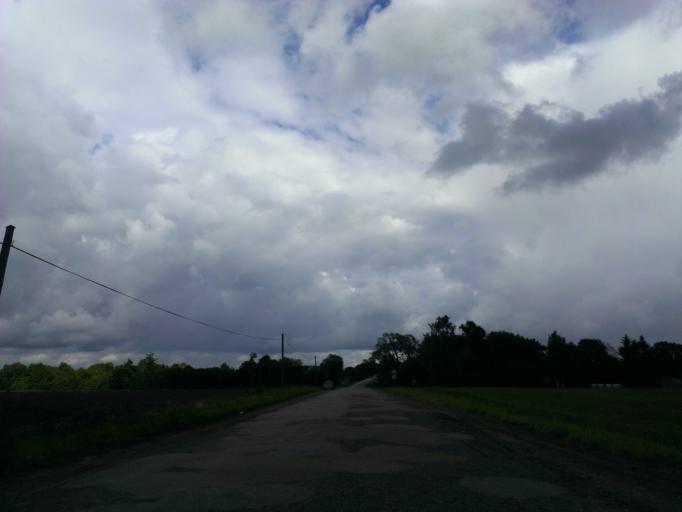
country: LV
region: Sigulda
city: Sigulda
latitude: 57.1638
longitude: 24.9058
